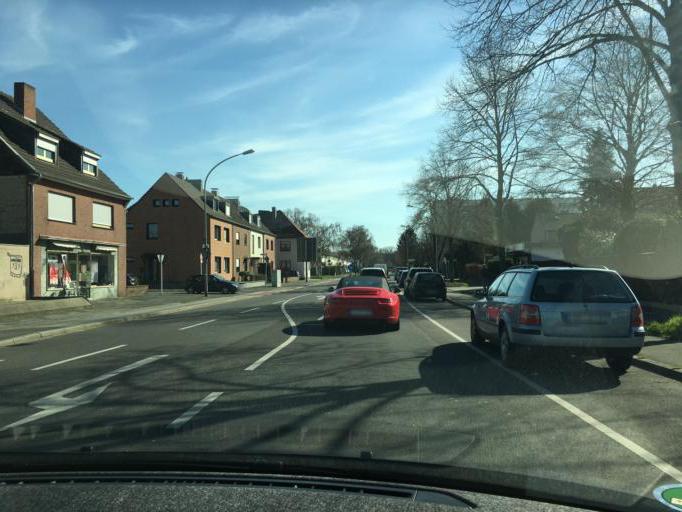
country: DE
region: North Rhine-Westphalia
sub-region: Regierungsbezirk Dusseldorf
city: Monchengladbach
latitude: 51.2035
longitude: 6.4745
